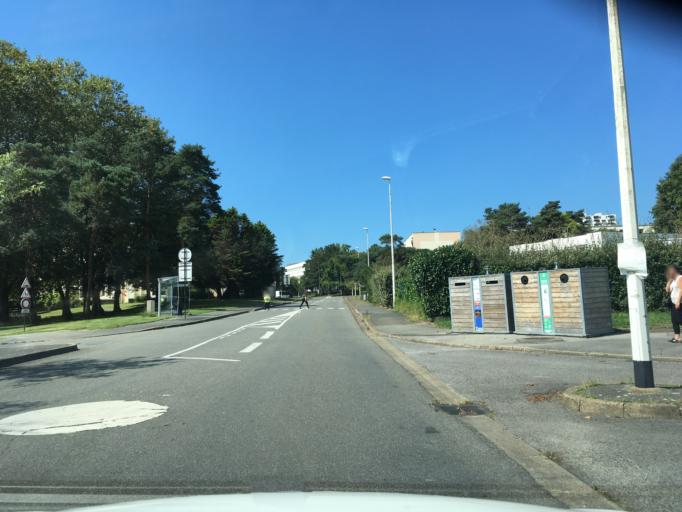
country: FR
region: Aquitaine
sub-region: Departement des Pyrenees-Atlantiques
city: Boucau
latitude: 43.4980
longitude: -1.4525
